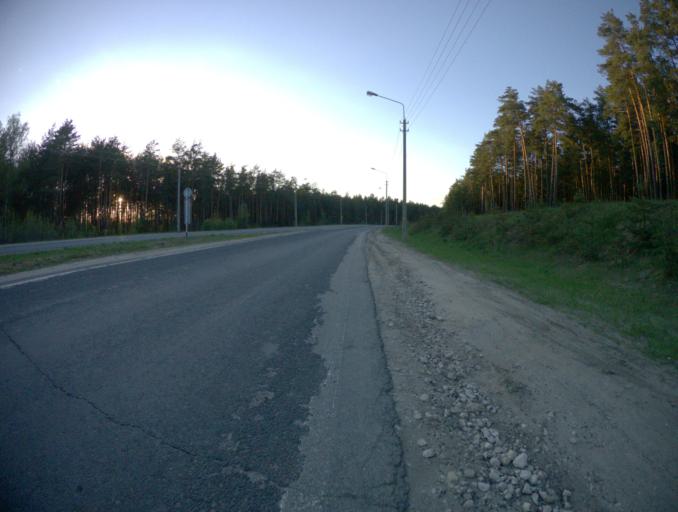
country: RU
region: Vladimir
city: Kommunar
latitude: 56.0643
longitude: 40.4329
